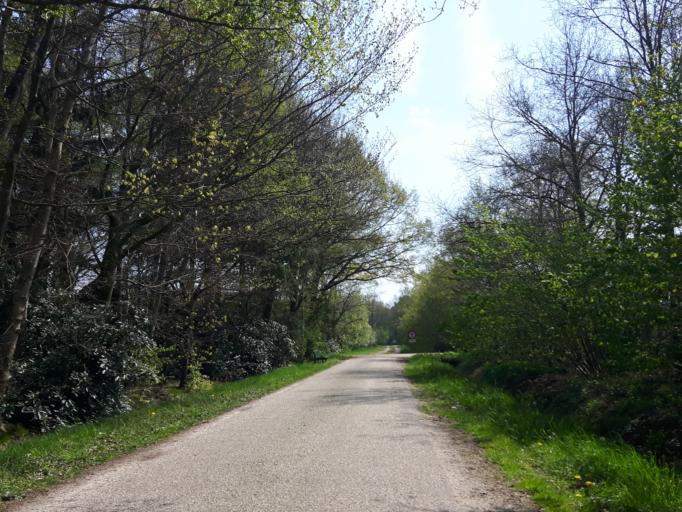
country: NL
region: Overijssel
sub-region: Gemeente Haaksbergen
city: Haaksbergen
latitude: 52.1274
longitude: 6.8179
